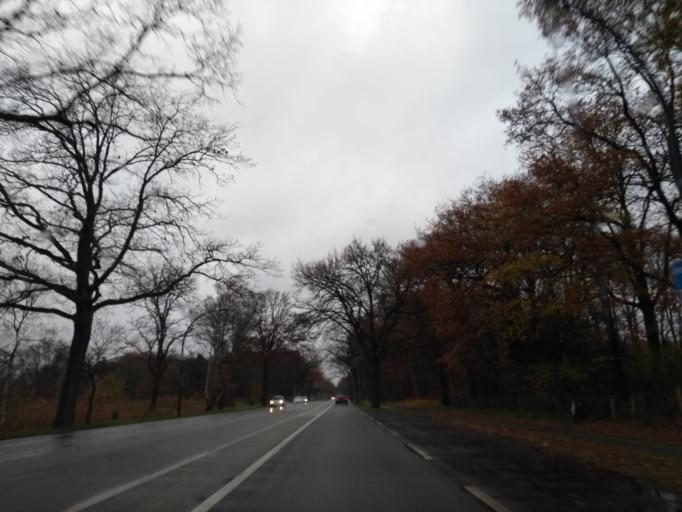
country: NL
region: Overijssel
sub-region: Gemeente Hengelo
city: Hengelo
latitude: 52.2480
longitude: 6.8276
